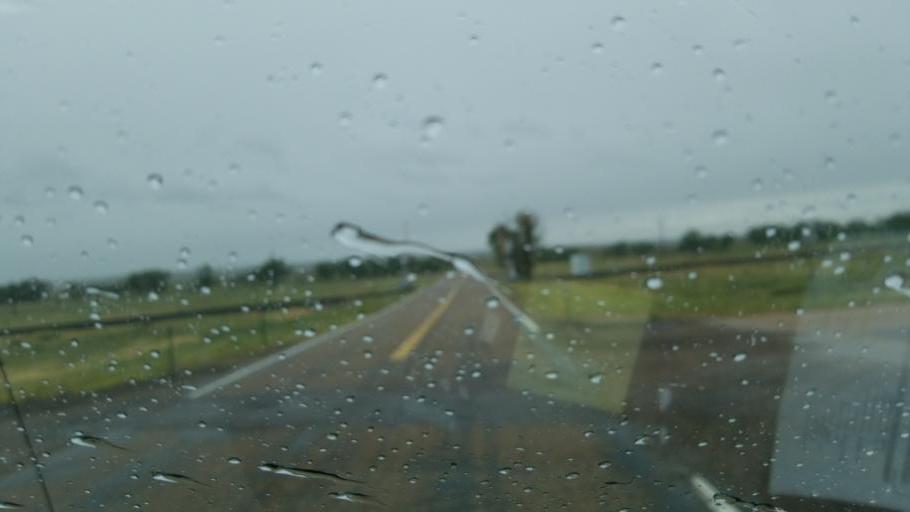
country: US
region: Colorado
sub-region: Lincoln County
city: Hugo
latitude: 38.8601
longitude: -103.1448
